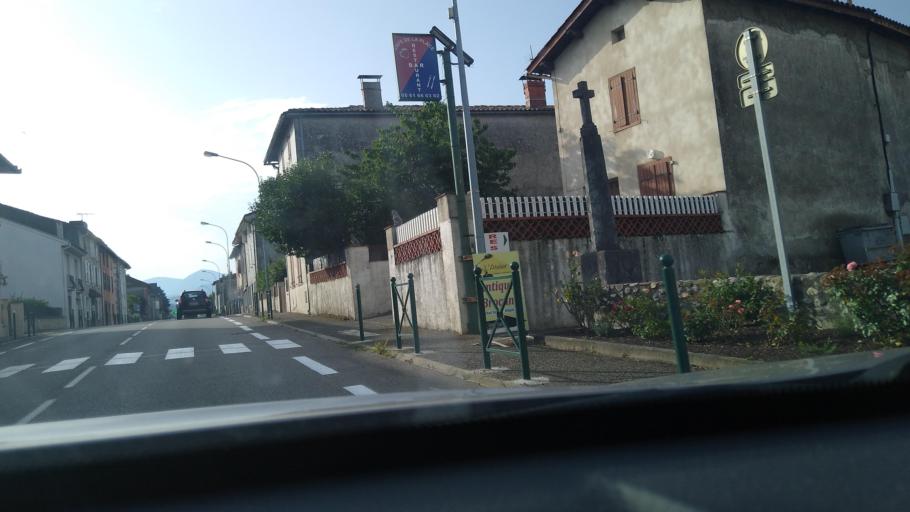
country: FR
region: Midi-Pyrenees
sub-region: Departement de l'Ariege
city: Saint-Lizier
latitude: 43.0095
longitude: 1.1192
